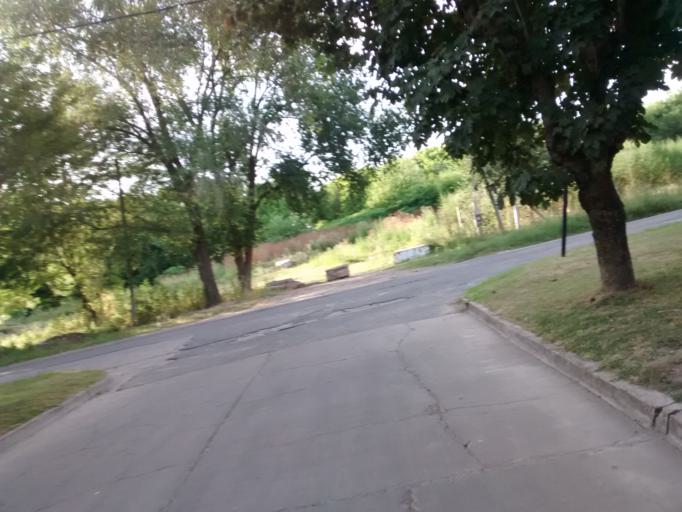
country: AR
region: Buenos Aires
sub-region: Partido de La Plata
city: La Plata
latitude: -34.8701
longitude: -58.0888
